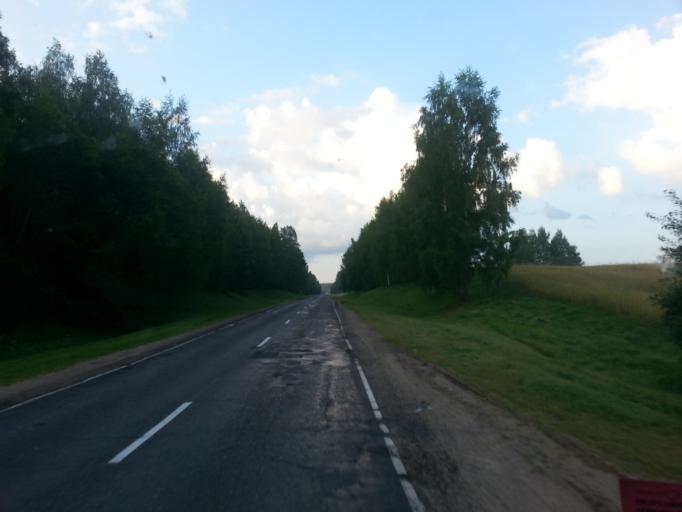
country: BY
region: Minsk
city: Kryvichy
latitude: 54.5809
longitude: 27.1987
